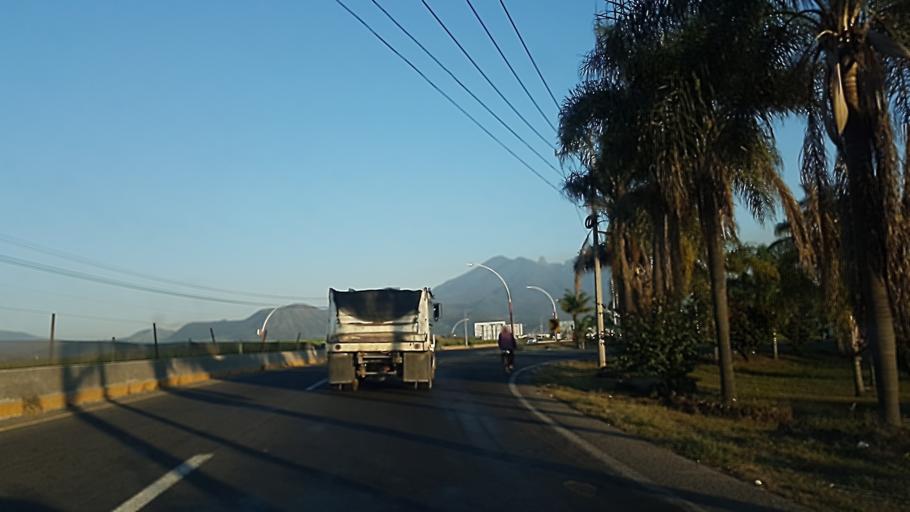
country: MX
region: Nayarit
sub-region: Tepic
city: La Corregidora
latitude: 21.4691
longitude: -104.8453
